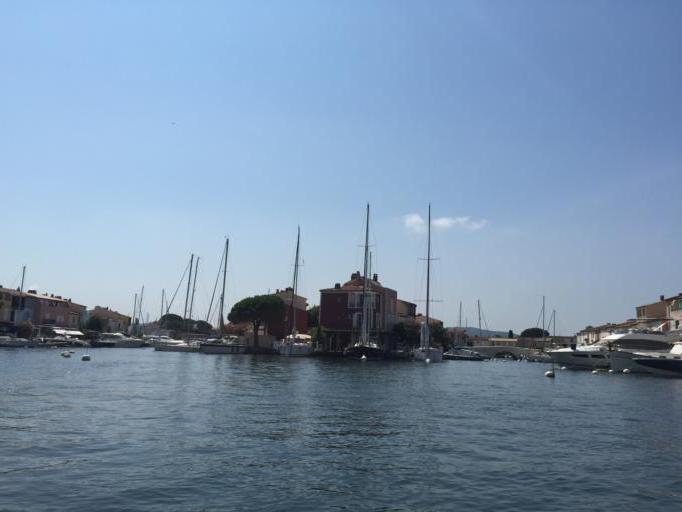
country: FR
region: Provence-Alpes-Cote d'Azur
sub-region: Departement du Var
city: Gassin
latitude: 43.2740
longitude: 6.5790
